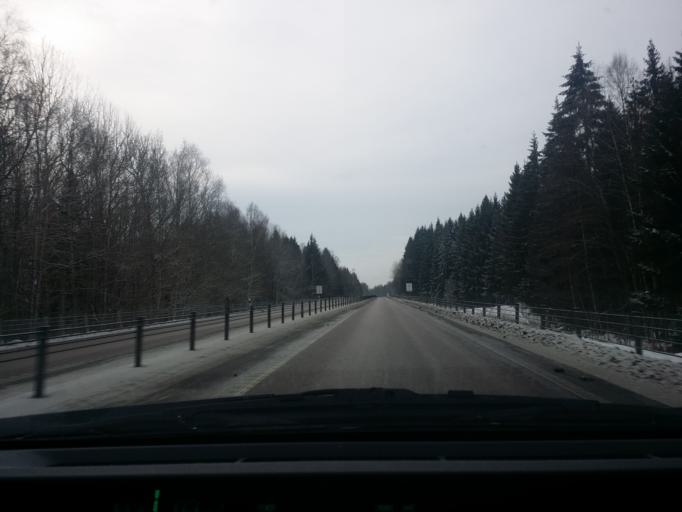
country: SE
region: Vaestra Goetaland
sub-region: Mariestads Kommun
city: Mariestad
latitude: 58.6059
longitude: 13.8021
